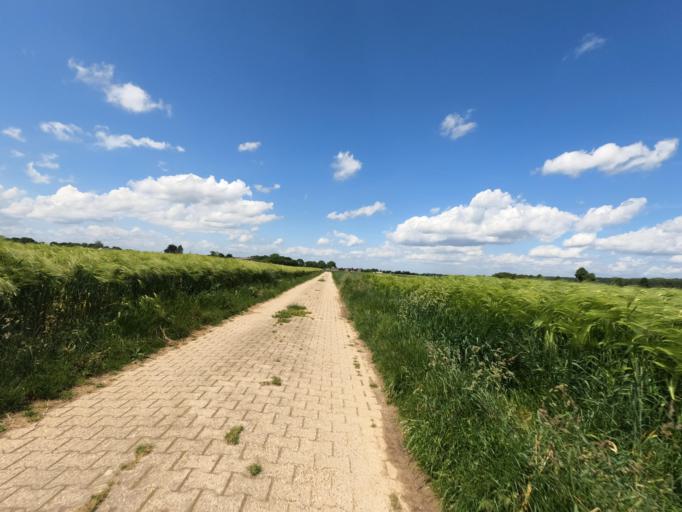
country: DE
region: North Rhine-Westphalia
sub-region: Regierungsbezirk Koln
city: Wassenberg
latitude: 51.0733
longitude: 6.1724
